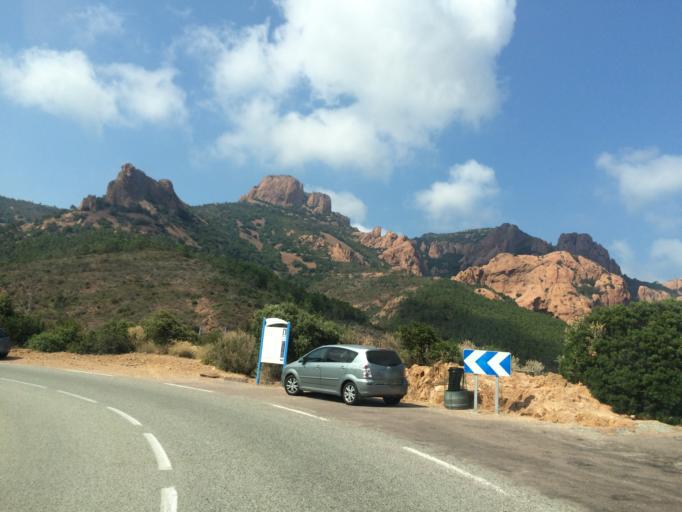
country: FR
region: Provence-Alpes-Cote d'Azur
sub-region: Departement des Alpes-Maritimes
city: Theoule-sur-Mer
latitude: 43.4409
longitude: 6.8988
